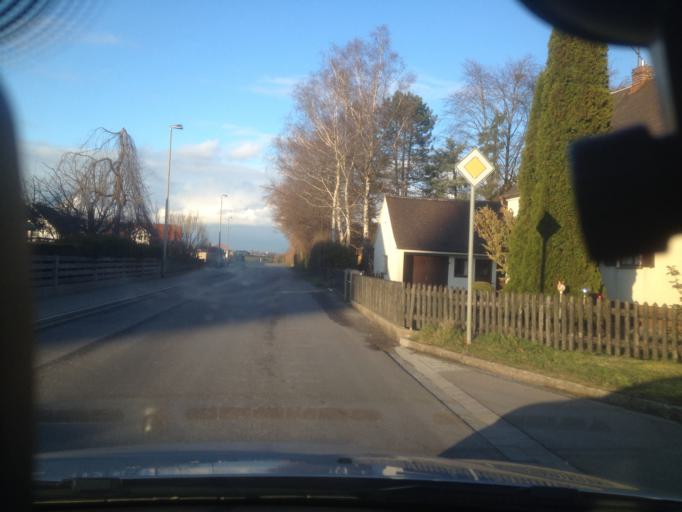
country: DE
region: Bavaria
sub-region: Upper Bavaria
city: Prittriching
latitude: 48.2049
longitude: 10.9320
